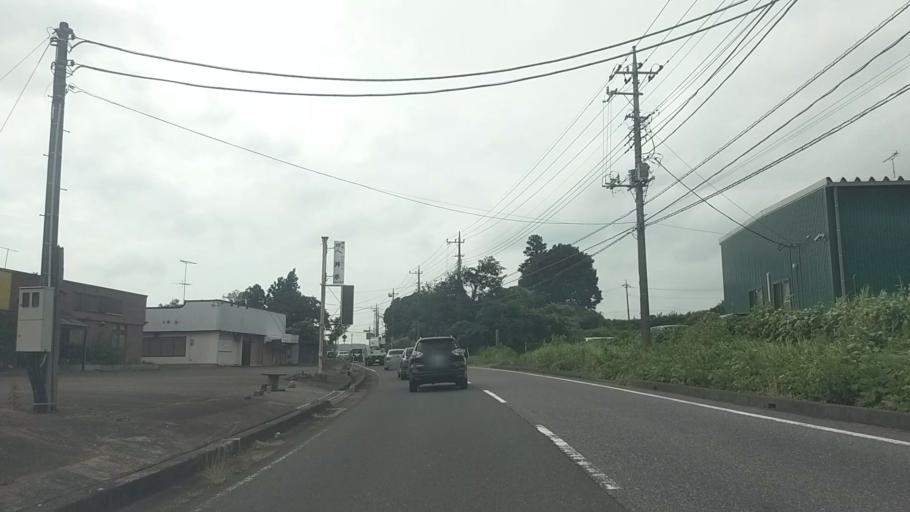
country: JP
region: Chiba
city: Kimitsu
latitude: 35.2764
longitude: 139.9934
